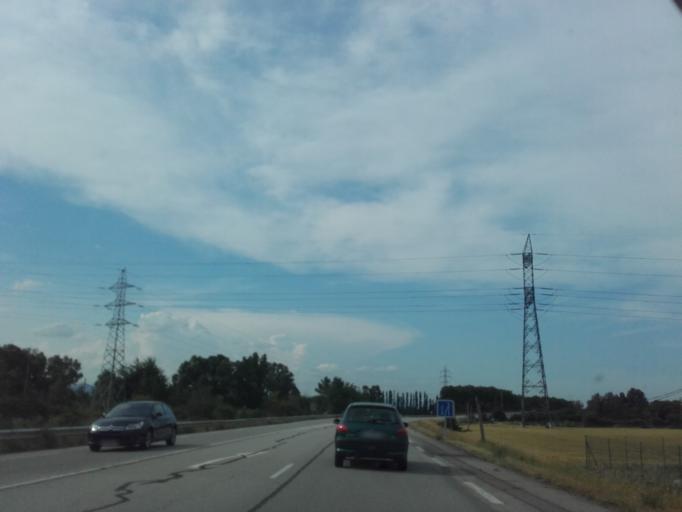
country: FR
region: Rhone-Alpes
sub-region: Departement de la Drome
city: Saulce-sur-Rhone
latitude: 44.6806
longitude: 4.7941
